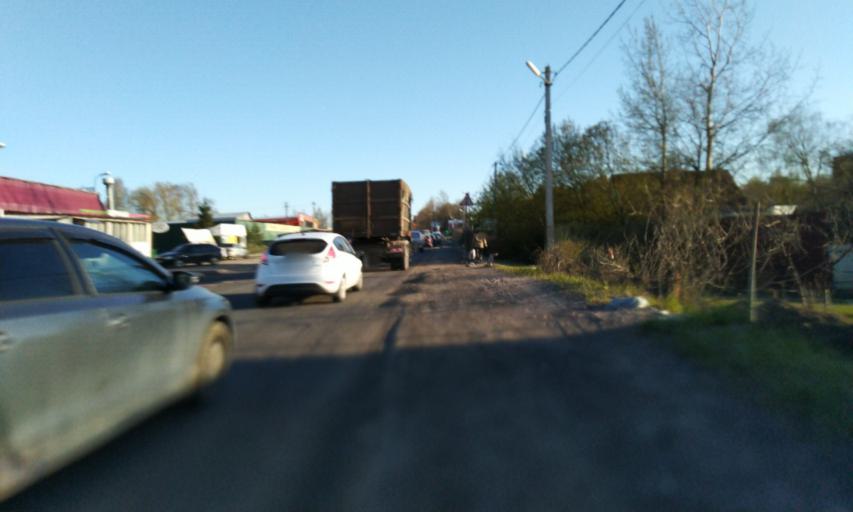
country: RU
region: Leningrad
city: Toksovo
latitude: 60.1137
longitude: 30.5025
